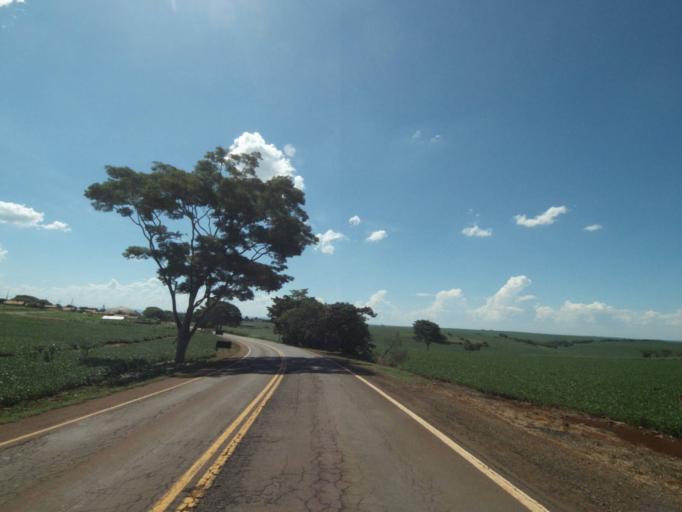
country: BR
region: Parana
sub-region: Sertanopolis
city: Sertanopolis
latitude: -23.0351
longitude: -50.8080
